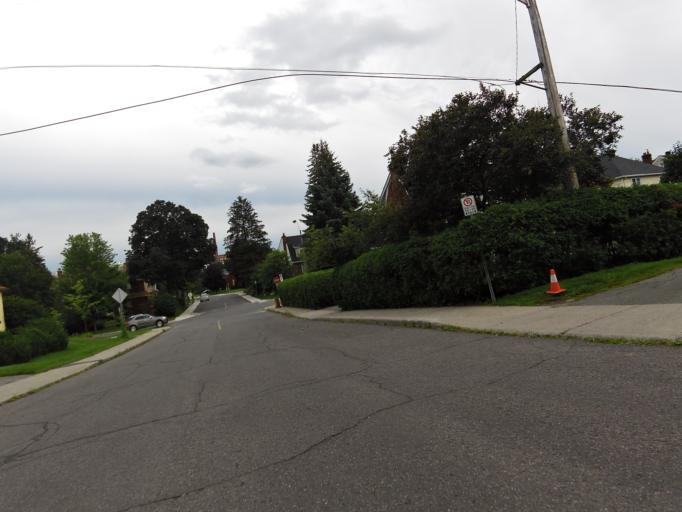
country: CA
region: Ontario
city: Ottawa
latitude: 45.3977
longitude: -75.7223
